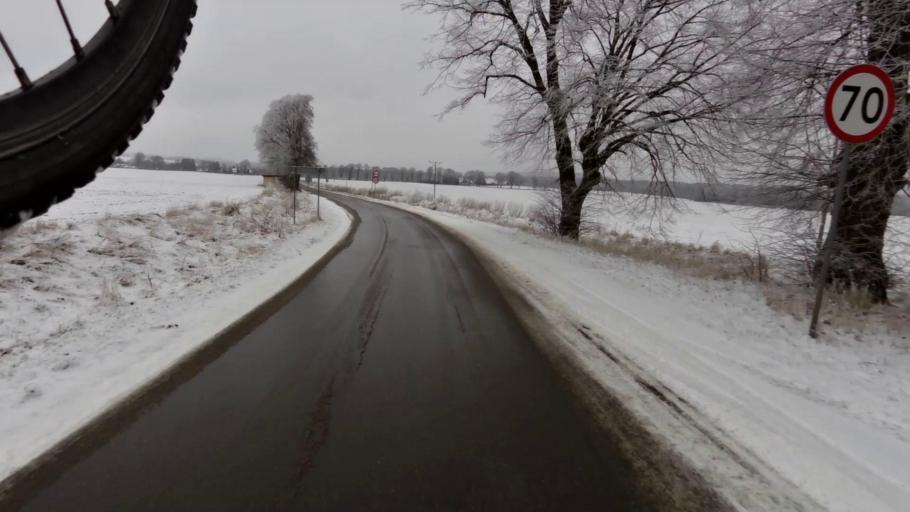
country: PL
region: West Pomeranian Voivodeship
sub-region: Powiat swidwinski
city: Rabino
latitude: 53.8482
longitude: 15.9622
